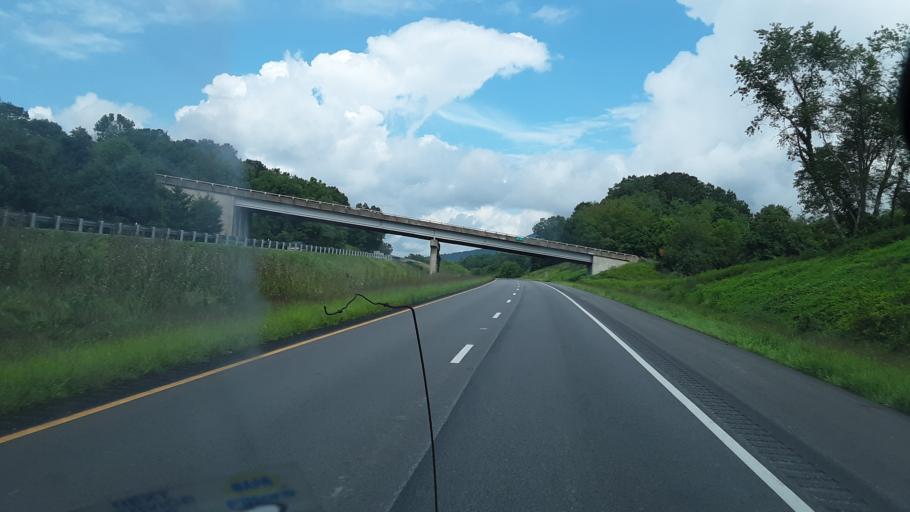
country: US
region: Virginia
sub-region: City of Lexington
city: Lexington
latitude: 37.8630
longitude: -79.4903
